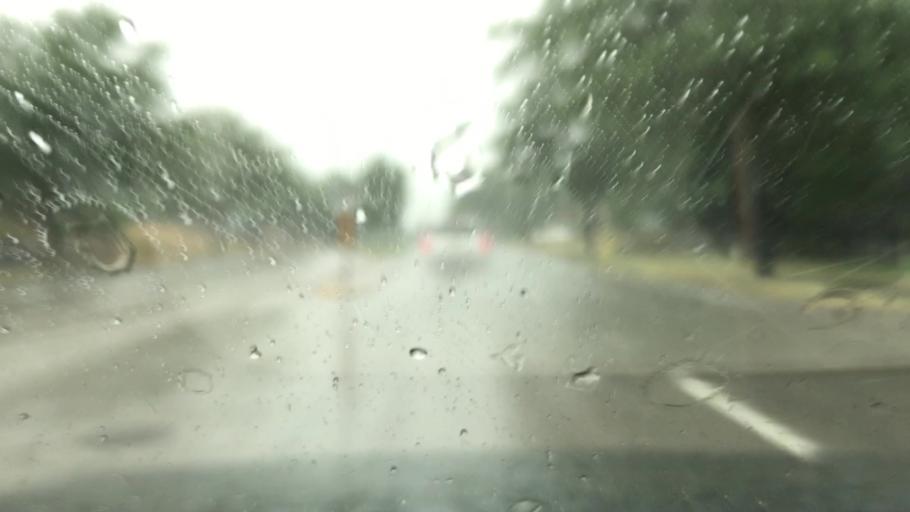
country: US
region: Michigan
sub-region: Kent County
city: Wyoming
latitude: 42.8824
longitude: -85.7241
